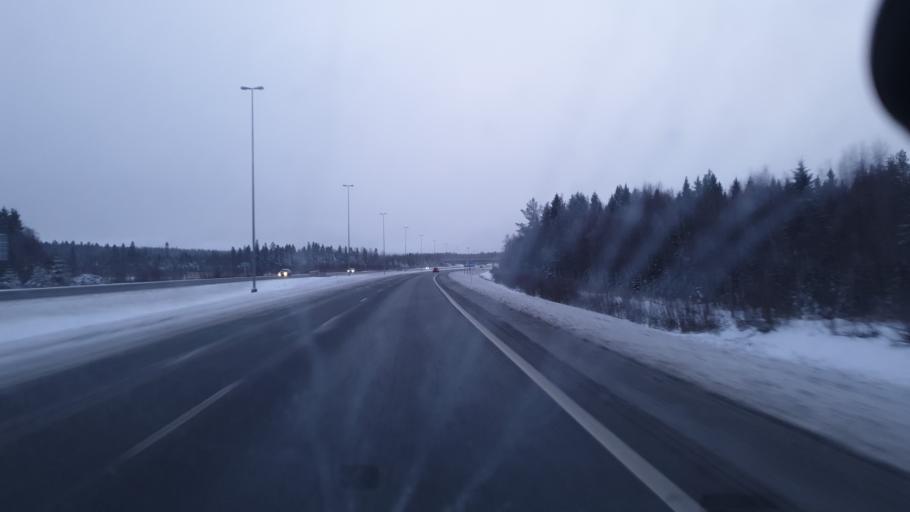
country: FI
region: Lapland
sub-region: Kemi-Tornio
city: Keminmaa
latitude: 65.8220
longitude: 24.4773
